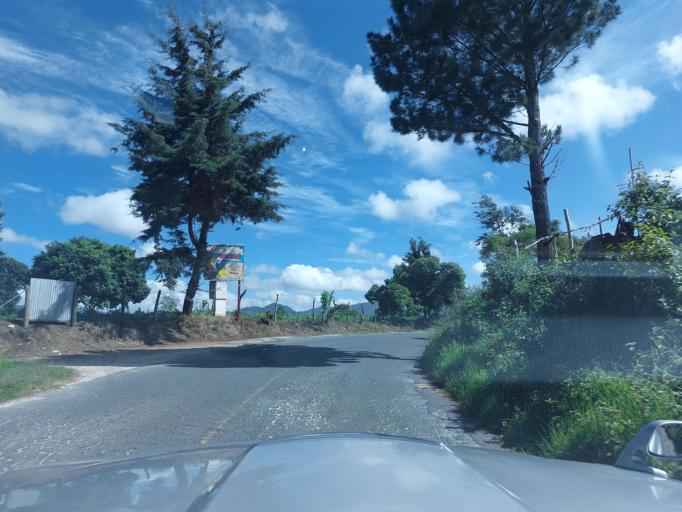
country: GT
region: Chimaltenango
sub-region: Municipio de San Juan Comalapa
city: Comalapa
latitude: 14.7212
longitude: -90.8891
